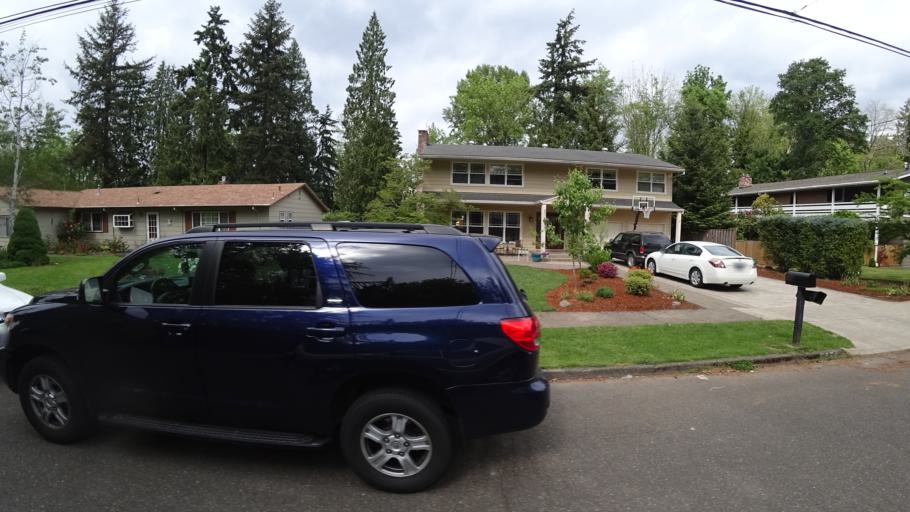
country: US
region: Oregon
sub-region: Washington County
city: Raleigh Hills
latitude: 45.4718
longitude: -122.7806
